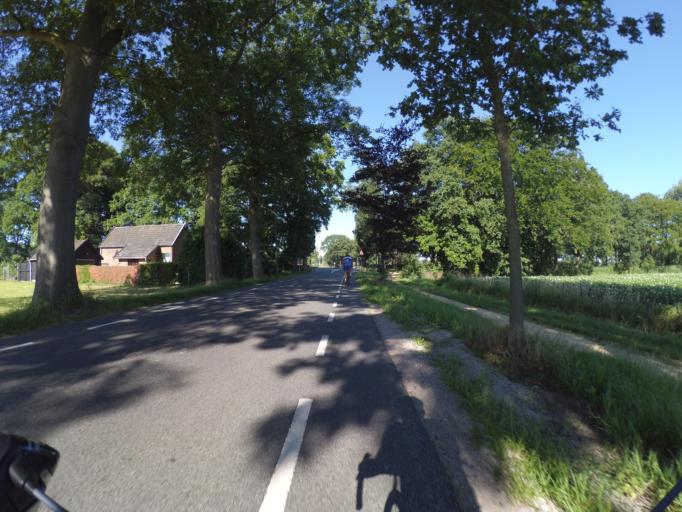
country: NL
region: North Brabant
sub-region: Gemeente Dongen
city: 's Gravenmoer
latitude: 51.6509
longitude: 4.9341
